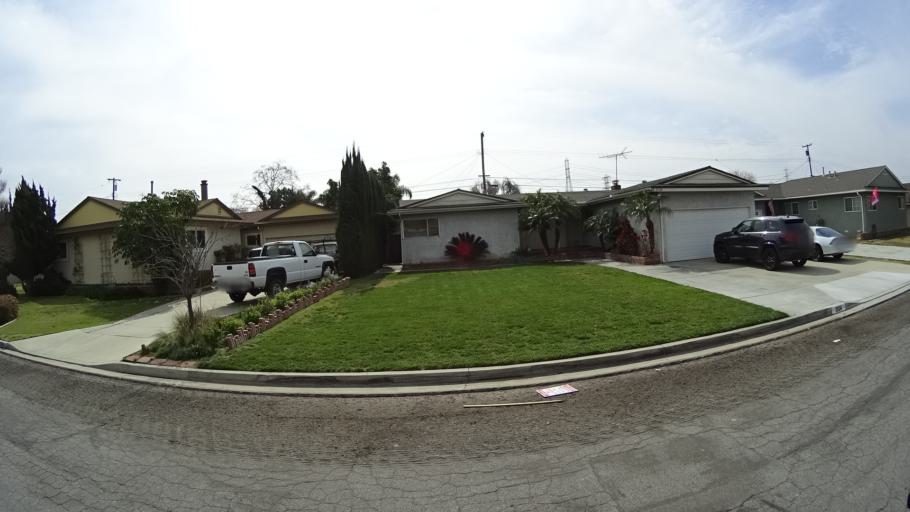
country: US
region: California
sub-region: Orange County
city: Stanton
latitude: 33.8094
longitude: -117.9564
